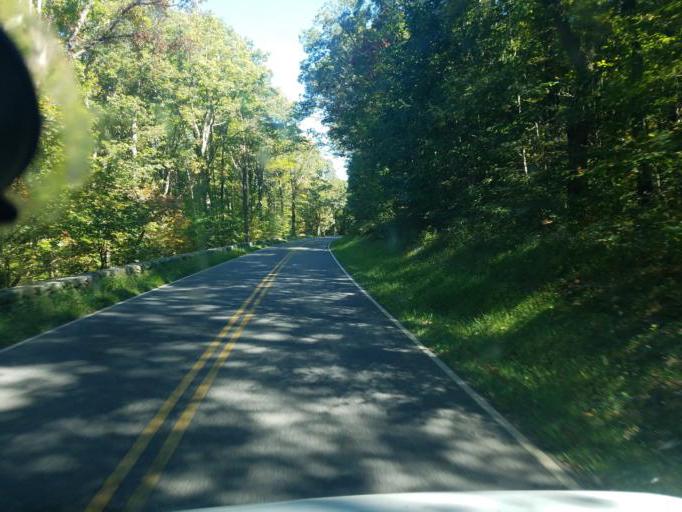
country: US
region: Virginia
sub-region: Rockingham County
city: Elkton
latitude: 38.3640
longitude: -78.5464
